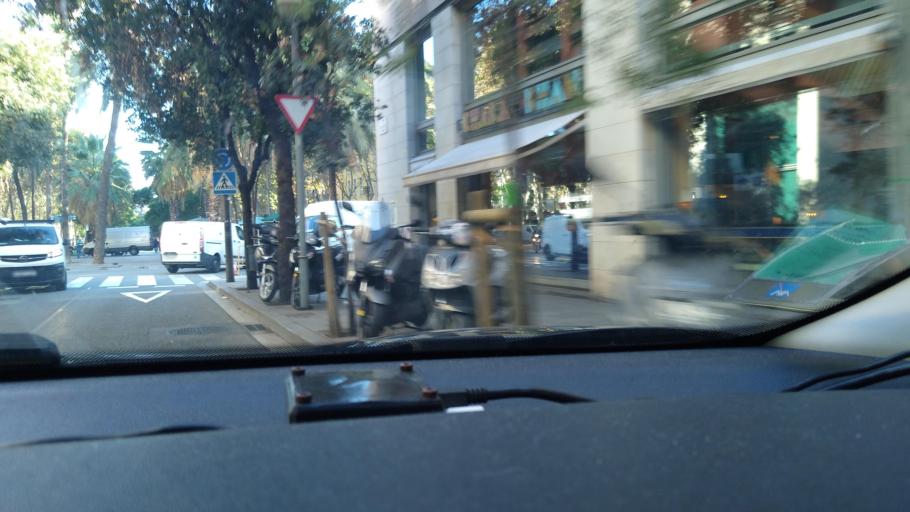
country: ES
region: Catalonia
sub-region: Provincia de Barcelona
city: Ciutat Vella
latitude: 41.3800
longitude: 2.1679
